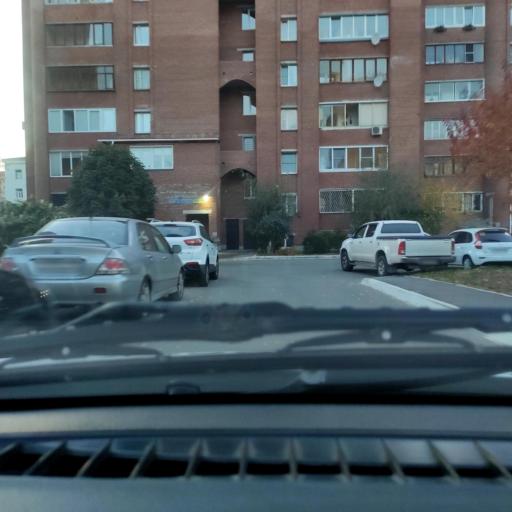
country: RU
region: Samara
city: Tol'yatti
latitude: 53.5029
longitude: 49.3948
